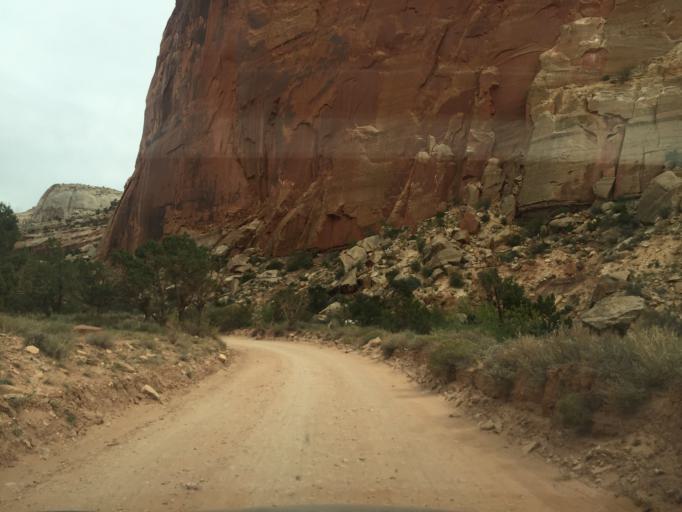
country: US
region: Utah
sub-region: Wayne County
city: Loa
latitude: 38.2598
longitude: -111.2231
